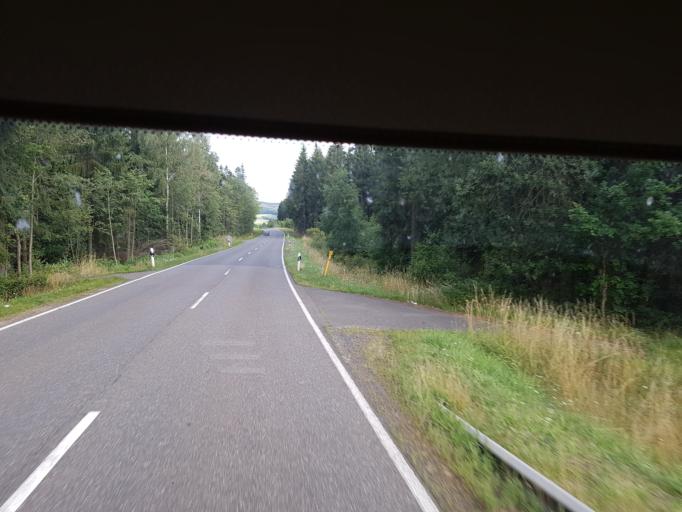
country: DE
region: Rheinland-Pfalz
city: Kradenbach
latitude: 50.2476
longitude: 6.8347
